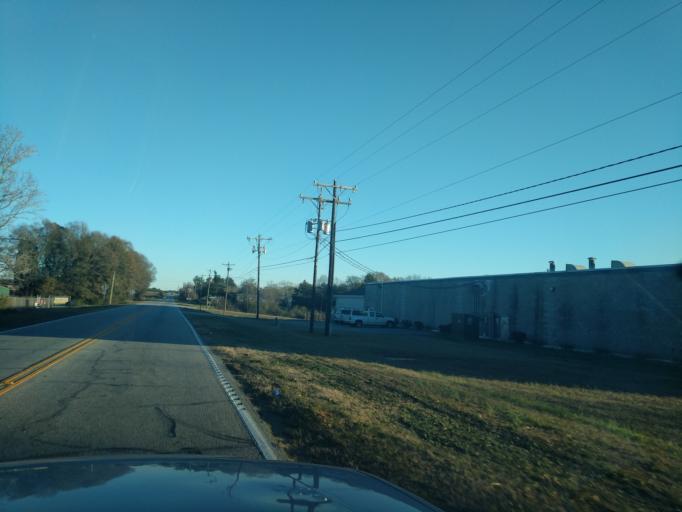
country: US
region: Georgia
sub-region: Hart County
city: Reed Creek
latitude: 34.5452
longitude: -82.8615
